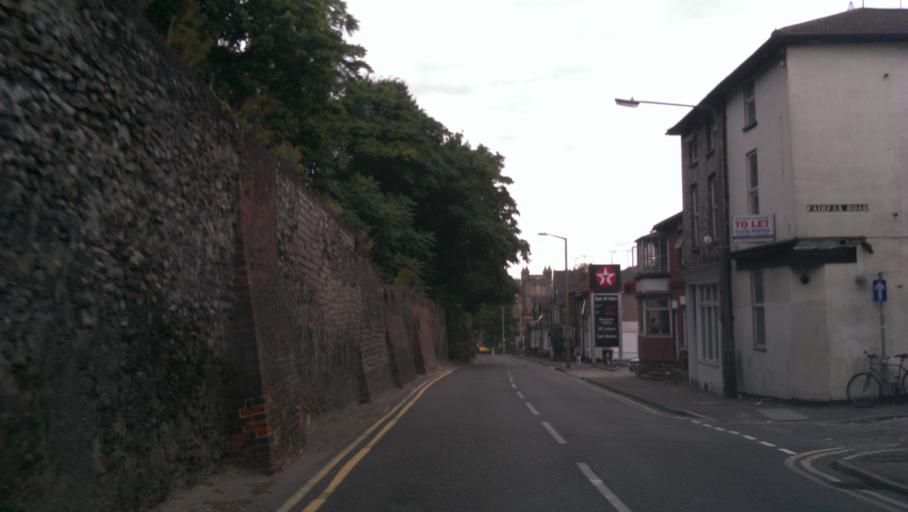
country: GB
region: England
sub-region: Essex
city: Colchester
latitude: 51.8840
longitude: 0.9031
